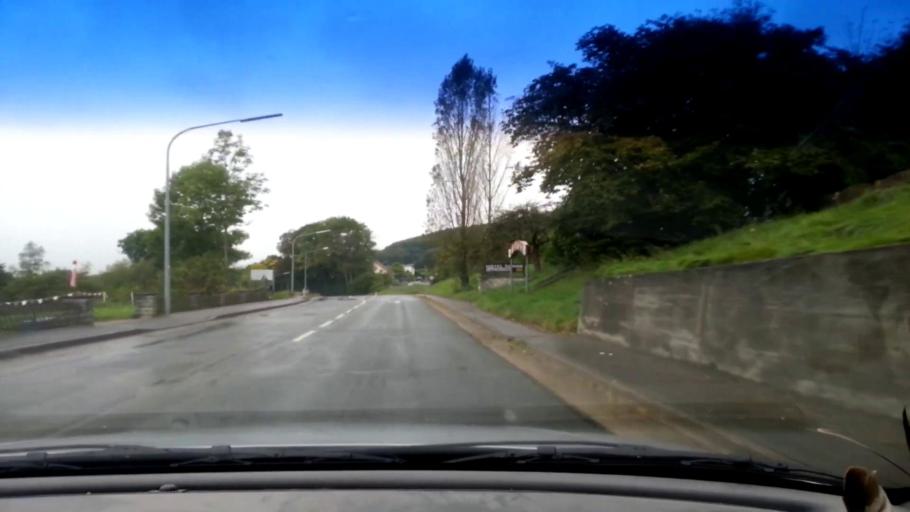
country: DE
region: Bavaria
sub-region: Upper Franconia
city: Schesslitz
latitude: 49.9800
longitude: 11.0862
